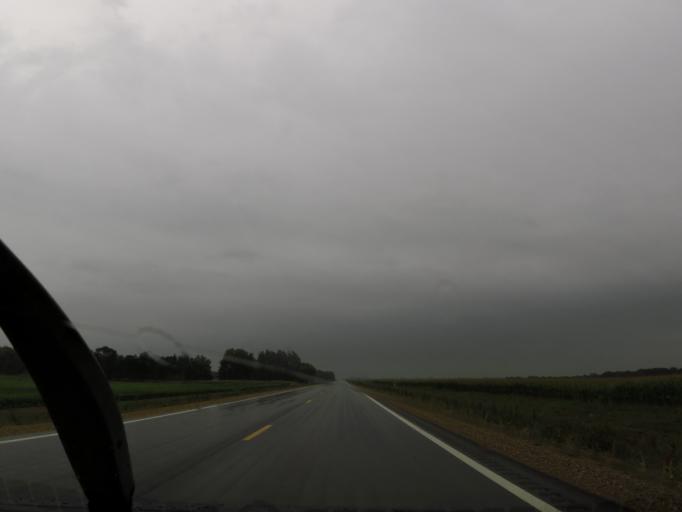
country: US
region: Minnesota
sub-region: Marshall County
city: Warren
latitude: 48.4562
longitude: -96.9281
